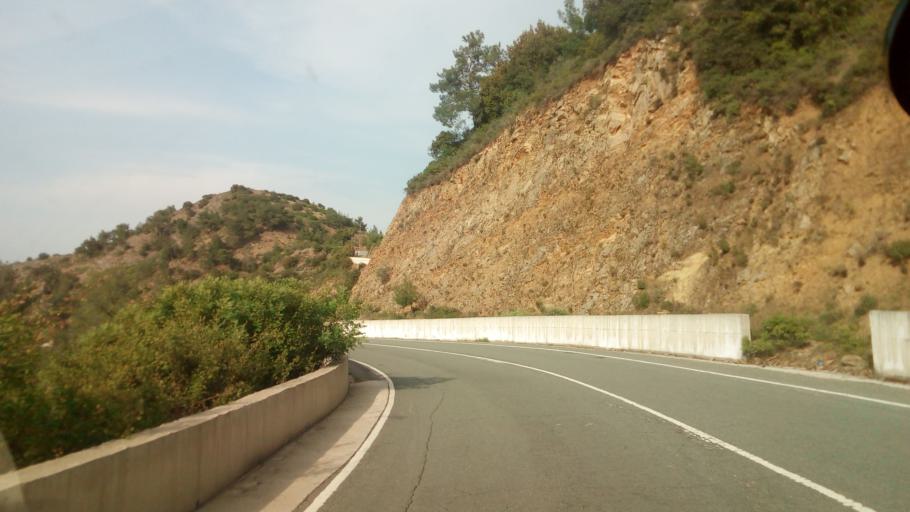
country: CY
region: Lefkosia
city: Kakopetria
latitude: 34.9988
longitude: 32.8081
